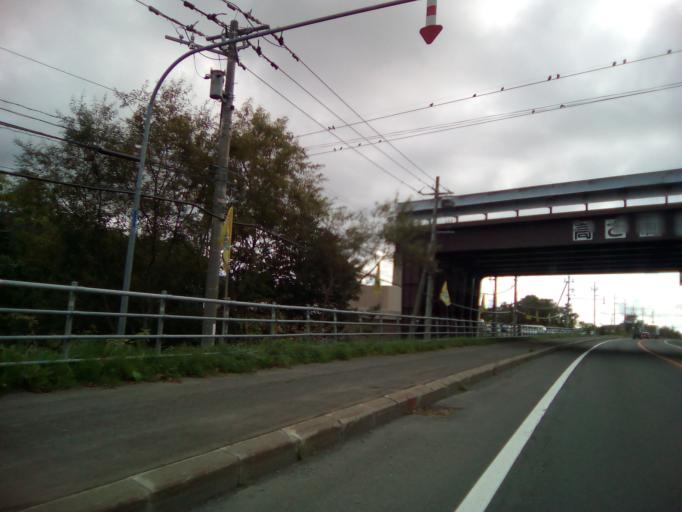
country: JP
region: Hokkaido
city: Niseko Town
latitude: 42.7488
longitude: 140.9013
